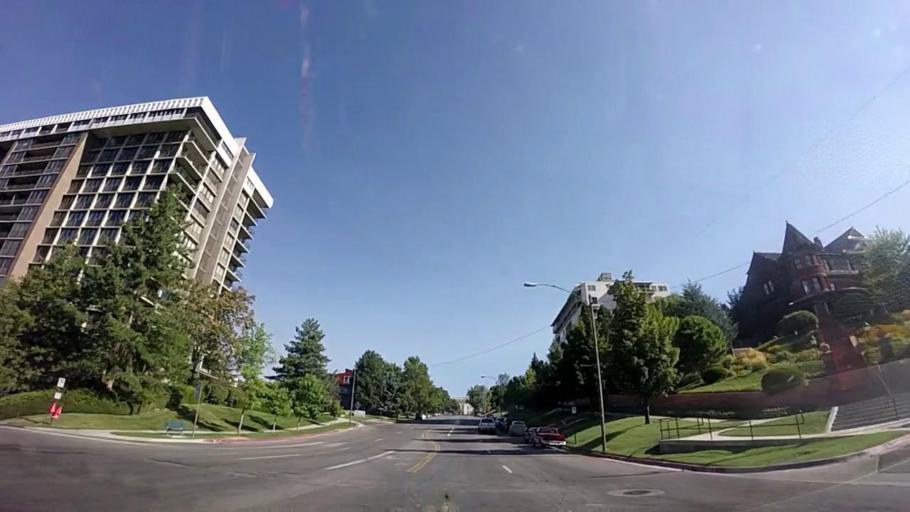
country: US
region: Utah
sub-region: Salt Lake County
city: Salt Lake City
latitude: 40.7736
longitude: -111.8911
